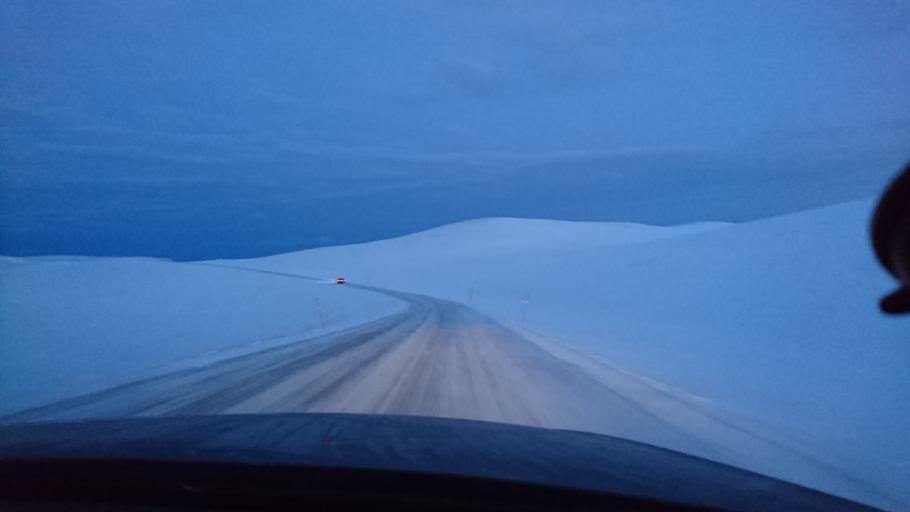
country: NO
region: Finnmark Fylke
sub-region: Nordkapp
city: Honningsvag
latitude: 71.0507
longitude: 25.7628
